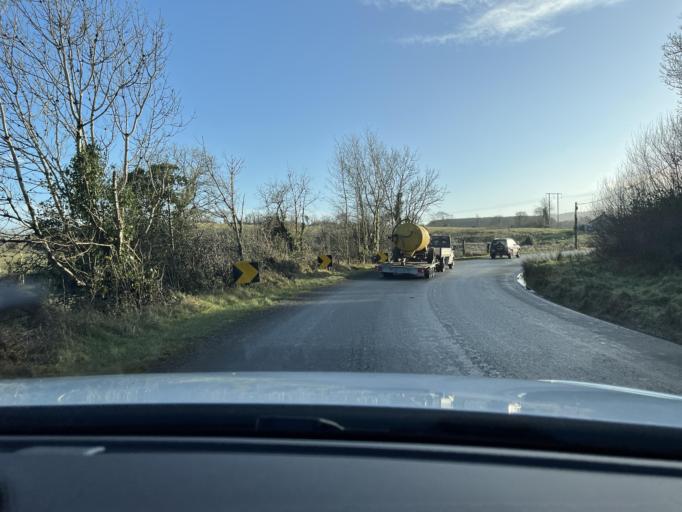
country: IE
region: Connaught
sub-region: County Leitrim
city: Manorhamilton
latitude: 54.1918
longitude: -8.1686
